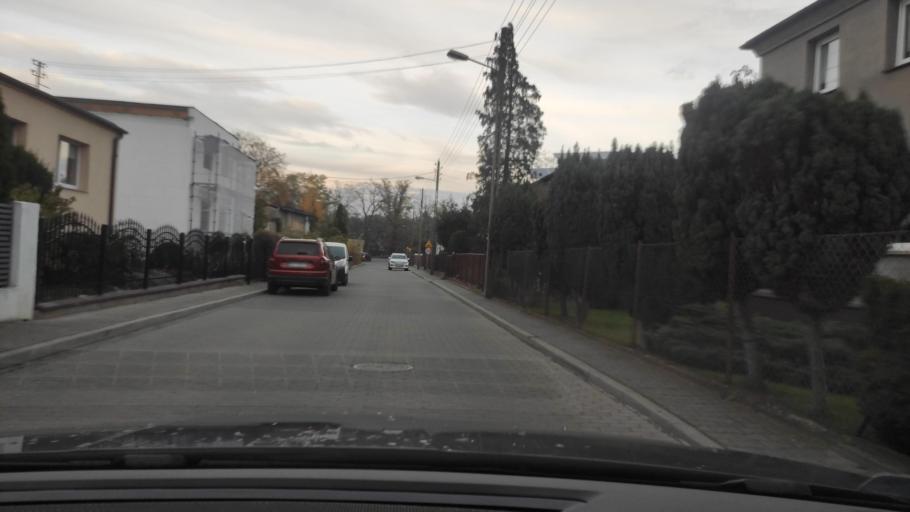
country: PL
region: Greater Poland Voivodeship
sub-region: Powiat poznanski
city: Swarzedz
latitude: 52.4087
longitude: 17.0684
